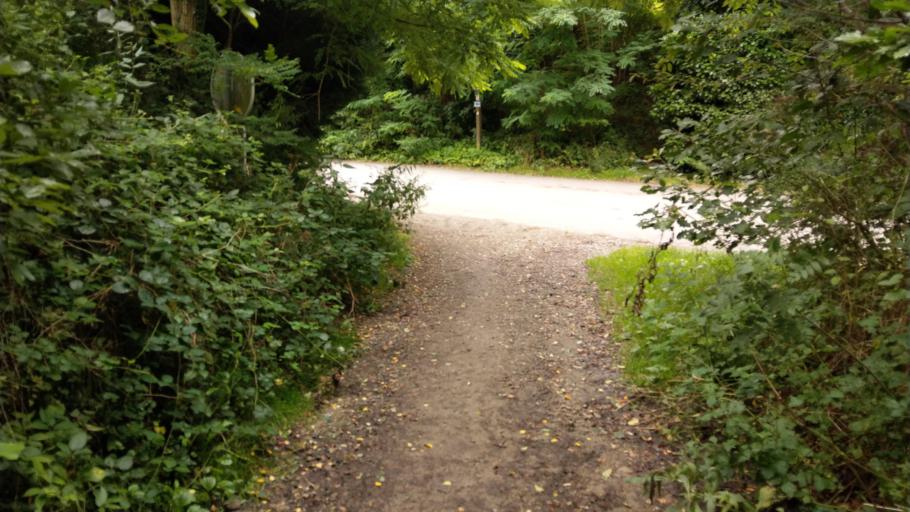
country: BE
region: Wallonia
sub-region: Province de Liege
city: La Calamine
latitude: 50.7329
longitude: 6.0055
